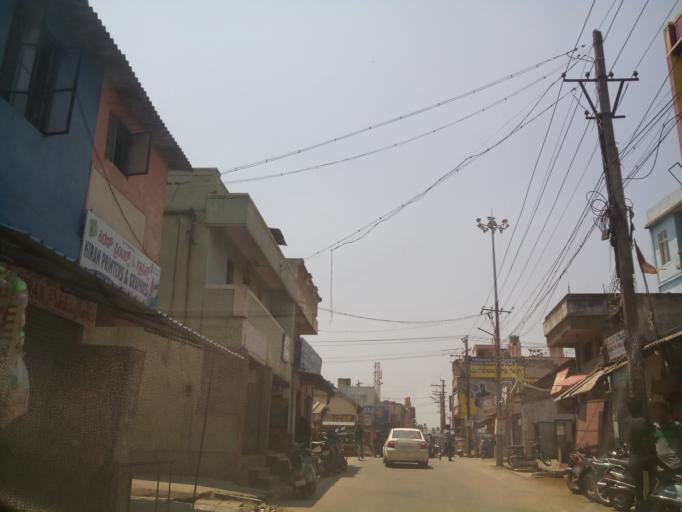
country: IN
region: Karnataka
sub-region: Hassan
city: Hassan
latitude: 13.0069
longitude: 76.0955
